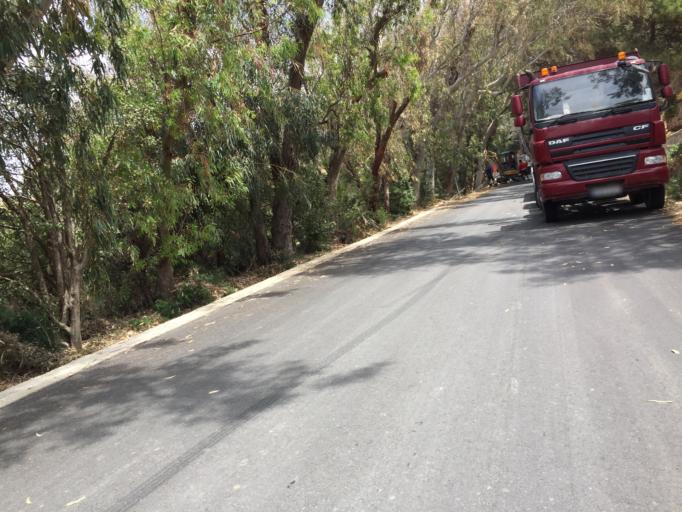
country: MT
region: Dingli
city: Dingli
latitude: 35.8812
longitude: 14.3440
